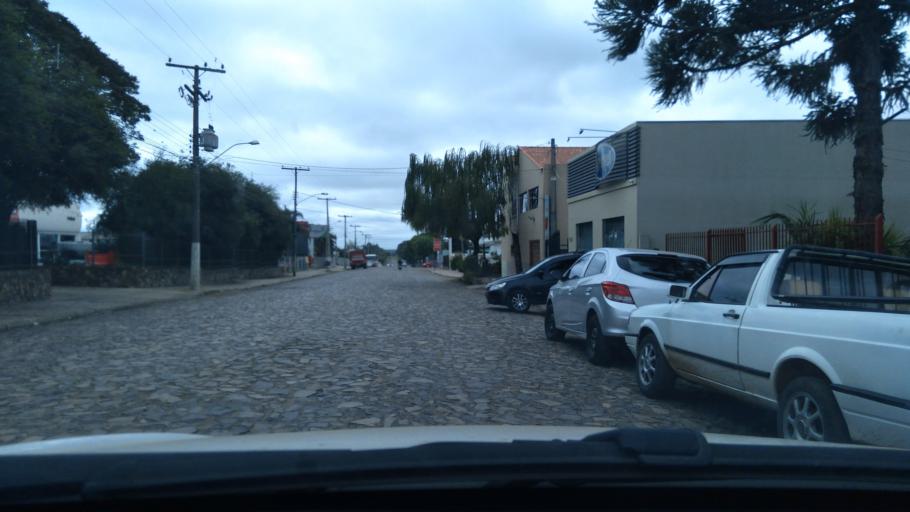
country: BR
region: Rio Grande do Sul
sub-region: Dom Pedrito
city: Dom Pedrito
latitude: -30.9661
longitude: -54.6730
